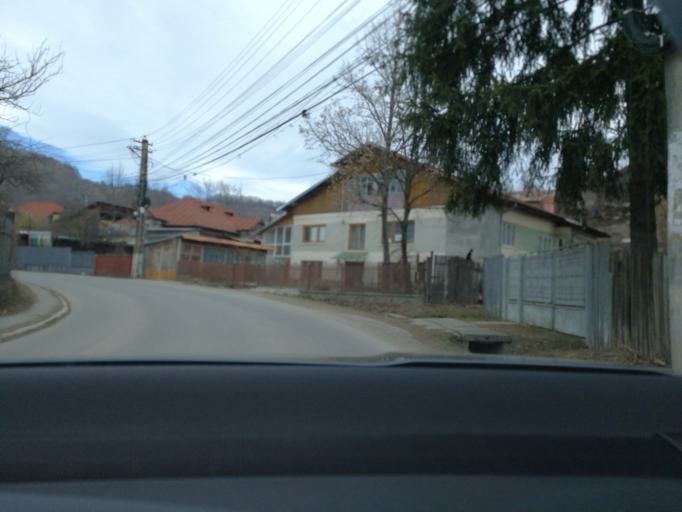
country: RO
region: Prahova
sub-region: Comuna Telega
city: Telega
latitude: 45.1382
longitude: 25.7879
